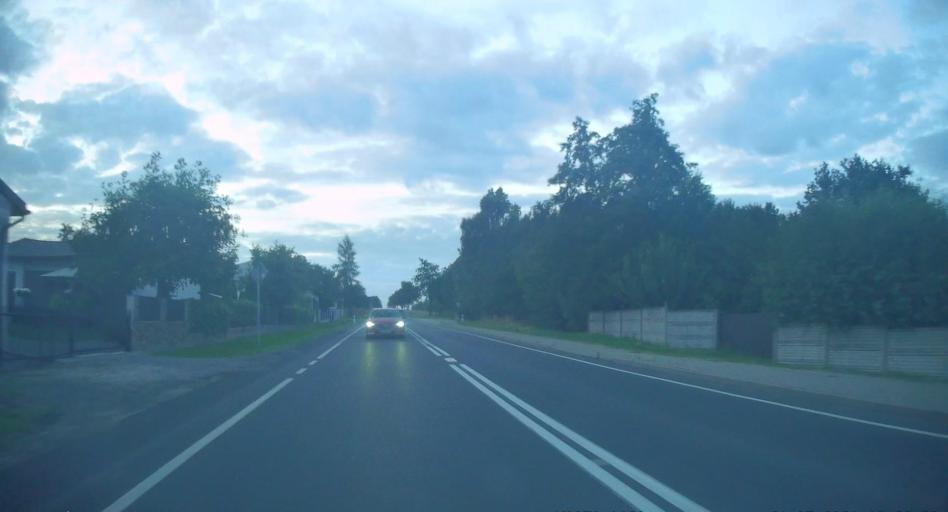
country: PL
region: Lodz Voivodeship
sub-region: Powiat wielunski
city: Patnow
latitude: 51.1469
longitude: 18.6072
